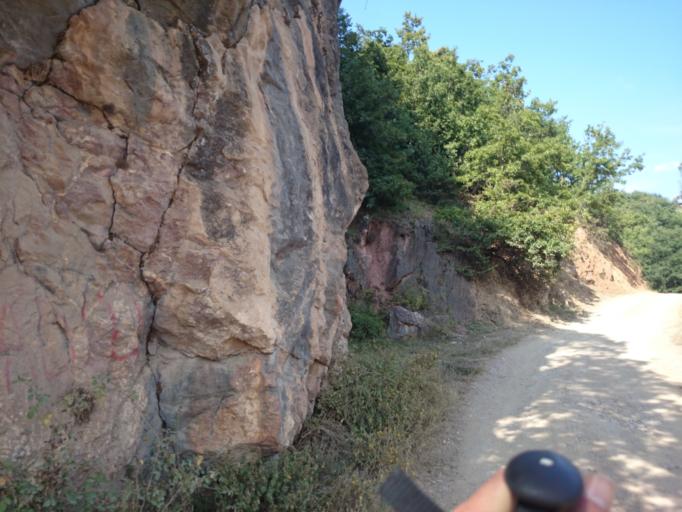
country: AL
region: Diber
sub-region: Rrethi i Dibres
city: Arras
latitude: 41.7392
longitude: 20.2979
